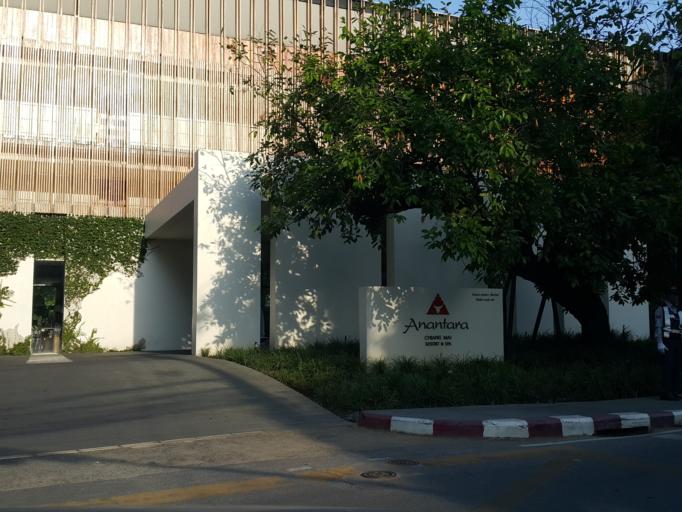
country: TH
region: Chiang Mai
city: Chiang Mai
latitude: 18.7816
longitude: 99.0035
